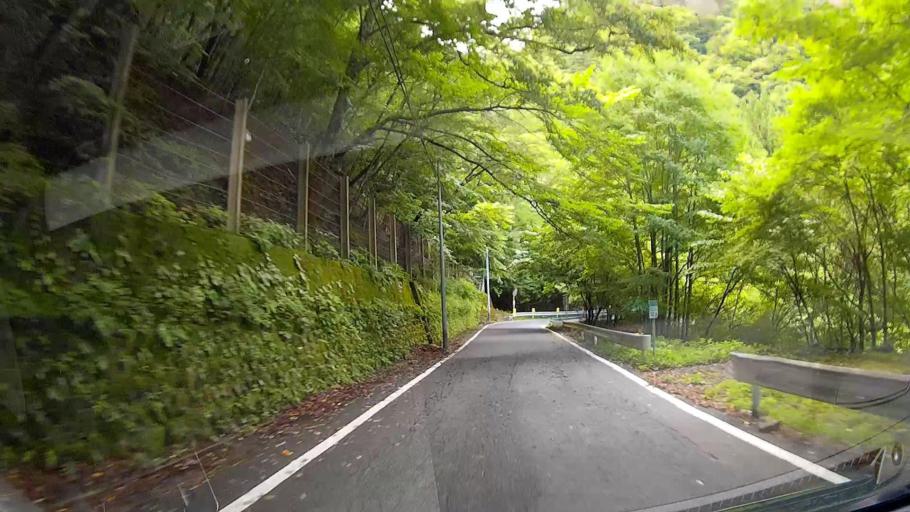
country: JP
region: Shizuoka
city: Shizuoka-shi
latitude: 35.2731
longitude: 138.2171
